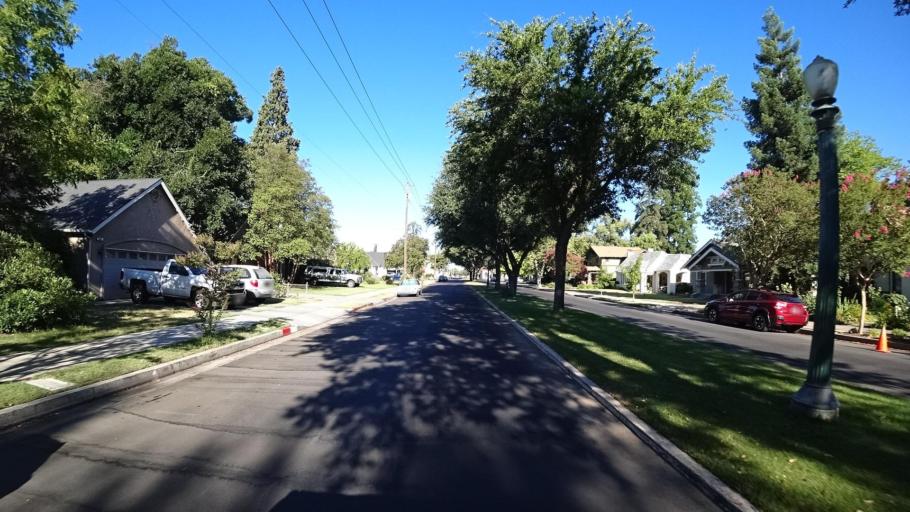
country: US
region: California
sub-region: Fresno County
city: Fresno
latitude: 36.7685
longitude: -119.8021
